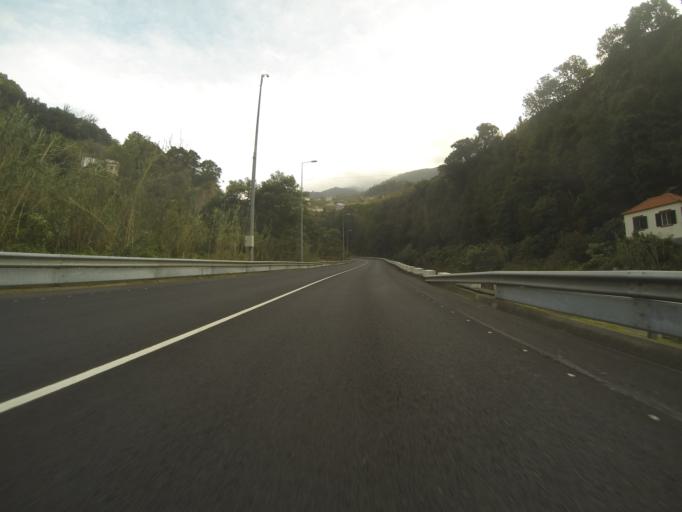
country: PT
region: Madeira
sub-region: Sao Vicente
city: Sao Vicente
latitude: 32.7966
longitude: -17.0402
